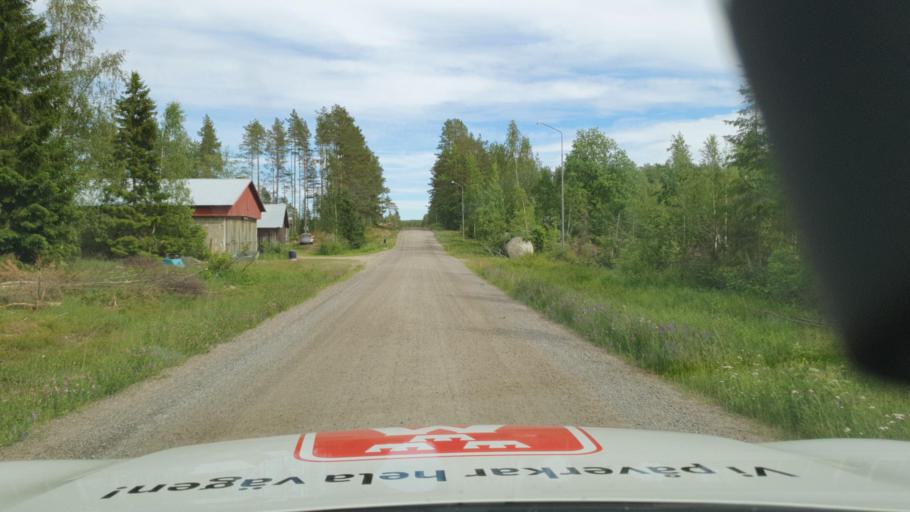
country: SE
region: Vaesterbotten
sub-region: Skelleftea Kommun
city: Burea
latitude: 64.3723
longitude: 21.0749
